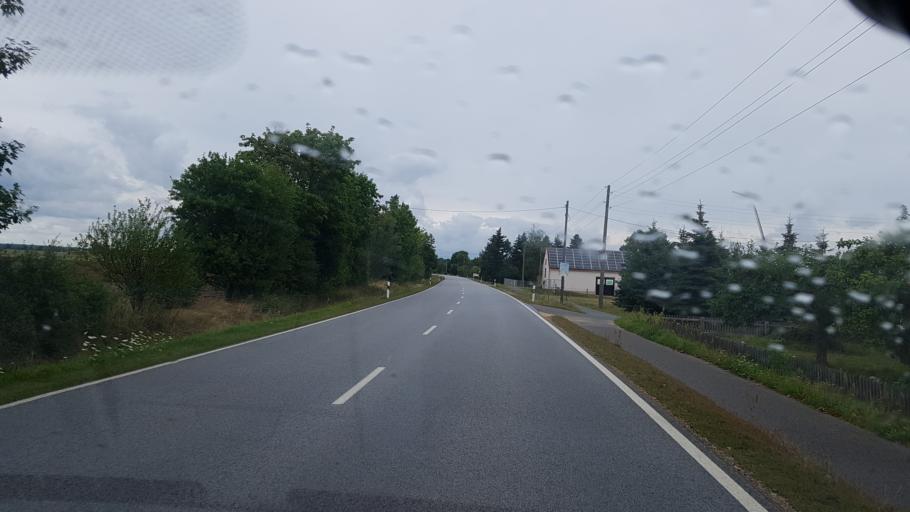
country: DE
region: Saxony
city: Niesky
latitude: 51.2340
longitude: 14.8036
